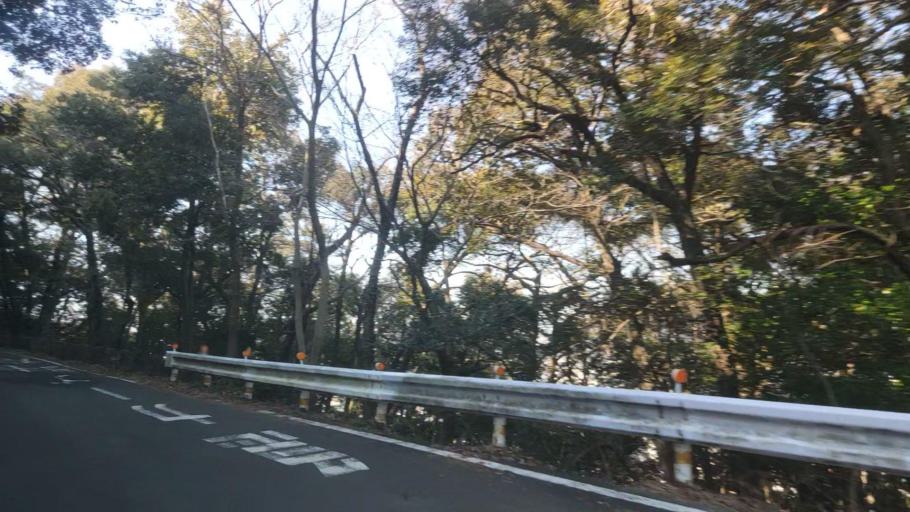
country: JP
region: Gifu
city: Gifu-shi
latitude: 35.4304
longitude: 136.7705
